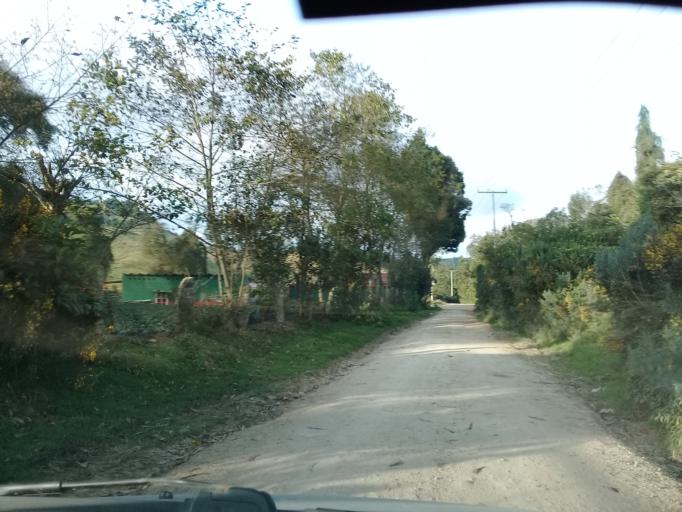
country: CO
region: Cundinamarca
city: Sibate
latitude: 4.4413
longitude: -74.2797
